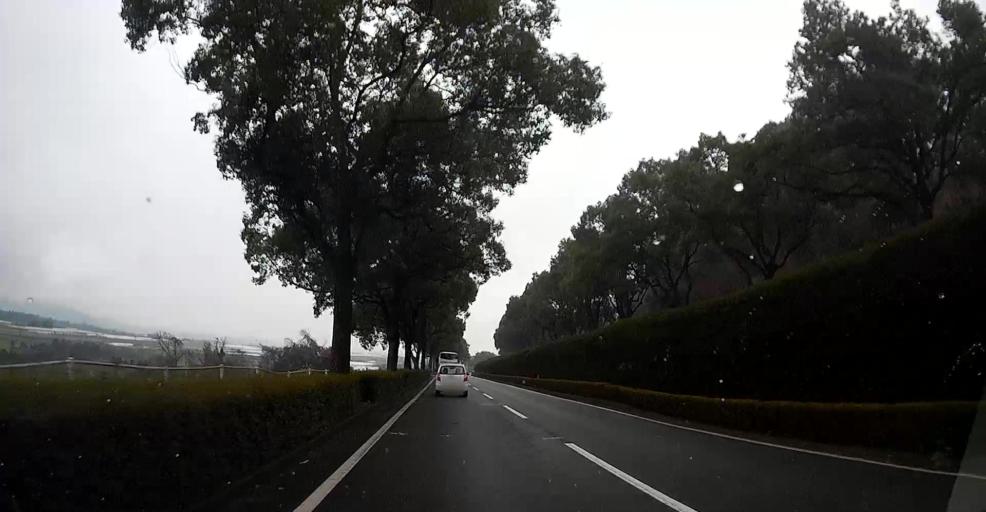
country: JP
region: Kumamoto
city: Ozu
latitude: 32.8171
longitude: 130.8412
